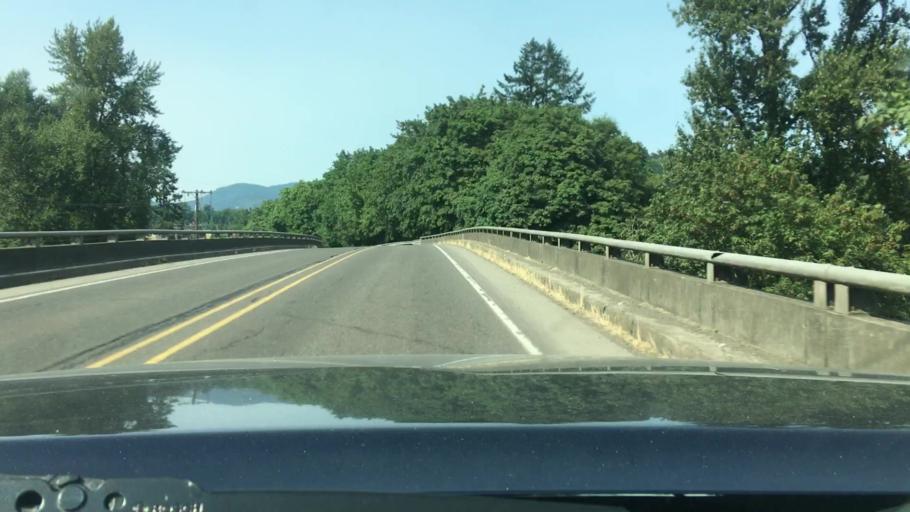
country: US
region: Oregon
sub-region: Lane County
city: Springfield
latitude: 44.0298
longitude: -123.0267
